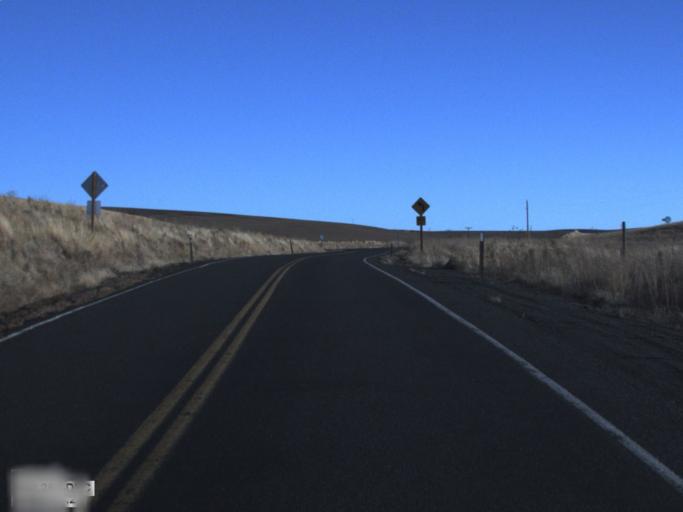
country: US
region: Washington
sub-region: Adams County
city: Ritzville
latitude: 46.6829
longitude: -118.3836
